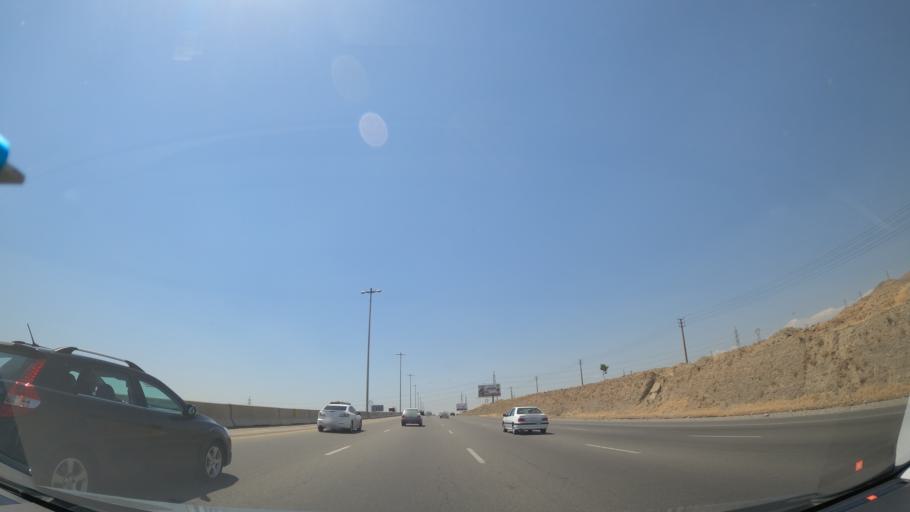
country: IR
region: Tehran
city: Shahr-e Qods
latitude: 35.7680
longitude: 51.0510
